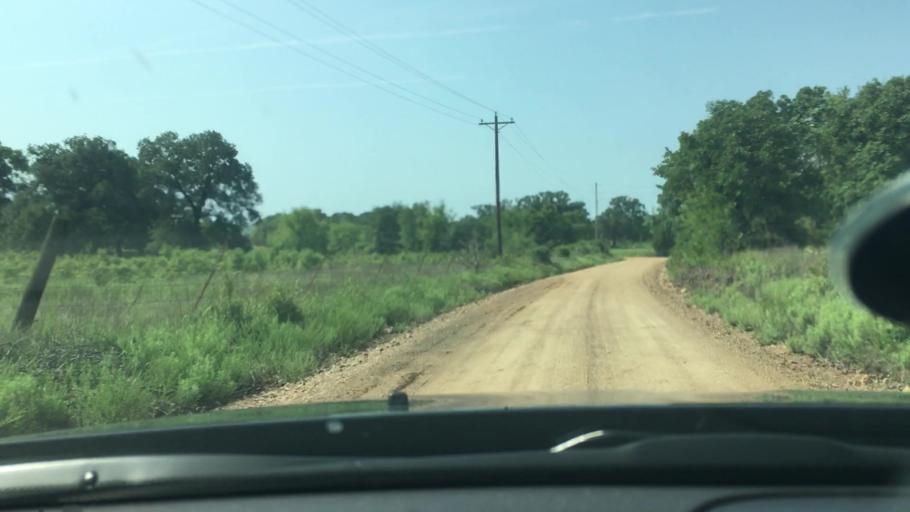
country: US
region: Oklahoma
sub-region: Atoka County
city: Atoka
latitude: 34.4429
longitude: -96.0547
